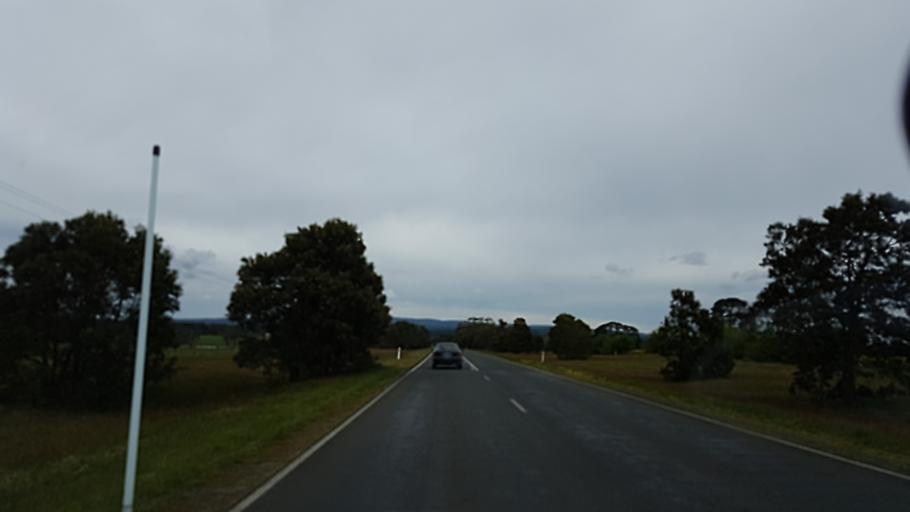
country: AU
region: Victoria
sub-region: Moorabool
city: Bacchus Marsh
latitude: -37.6156
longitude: 144.2127
